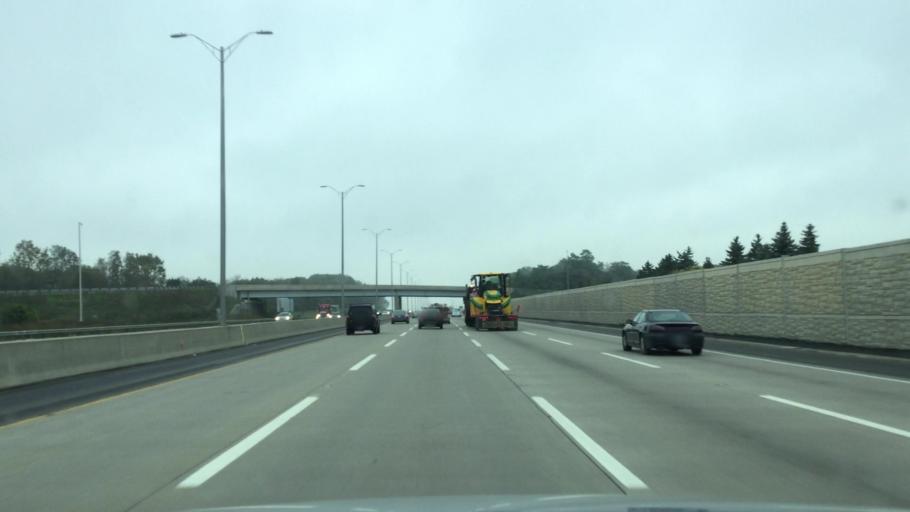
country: US
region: Illinois
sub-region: Lake County
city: Park City
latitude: 42.3342
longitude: -87.9128
